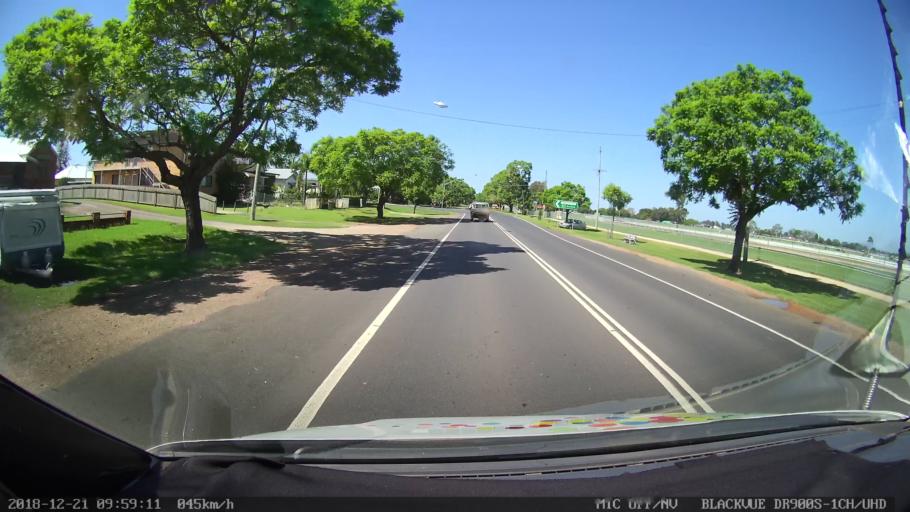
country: AU
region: New South Wales
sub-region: Clarence Valley
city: Grafton
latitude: -29.6767
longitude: 152.9321
